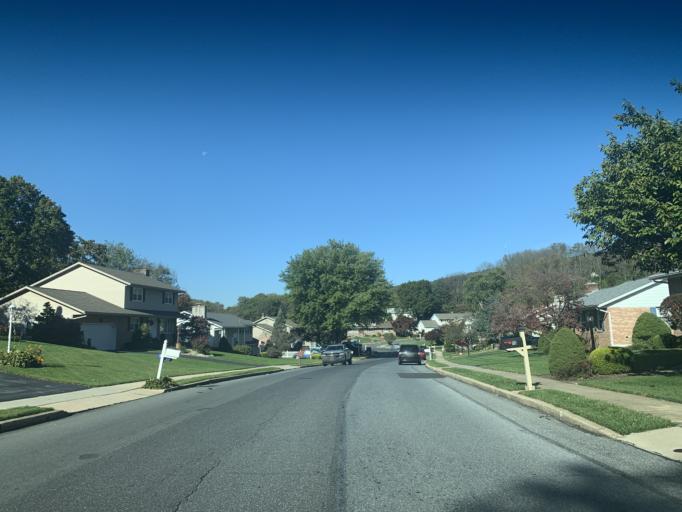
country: US
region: Pennsylvania
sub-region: Berks County
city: Reiffton
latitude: 40.3094
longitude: -75.8770
